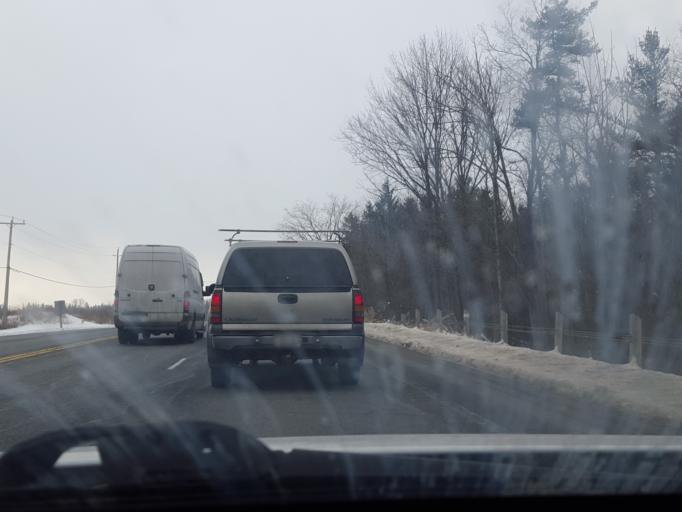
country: CA
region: Ontario
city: Vaughan
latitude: 43.9254
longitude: -79.5423
